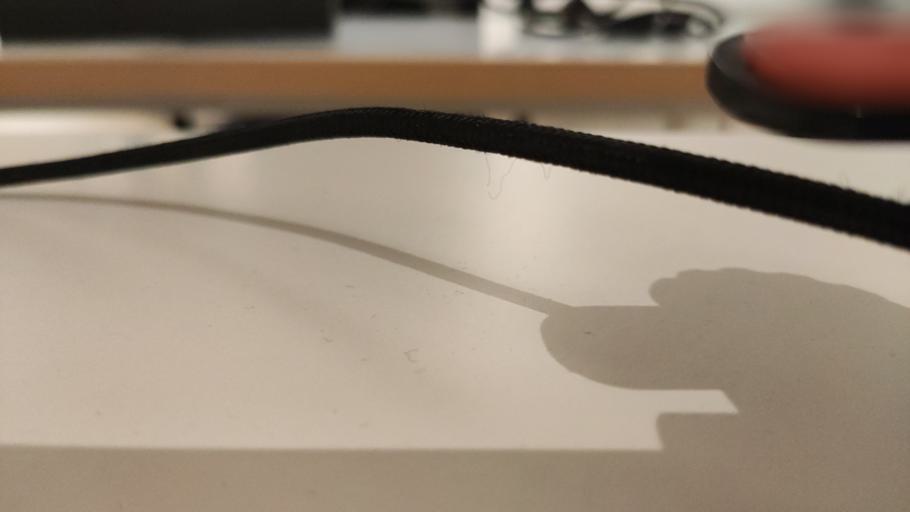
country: RU
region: Moskovskaya
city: Dorokhovo
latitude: 55.4533
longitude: 36.3527
